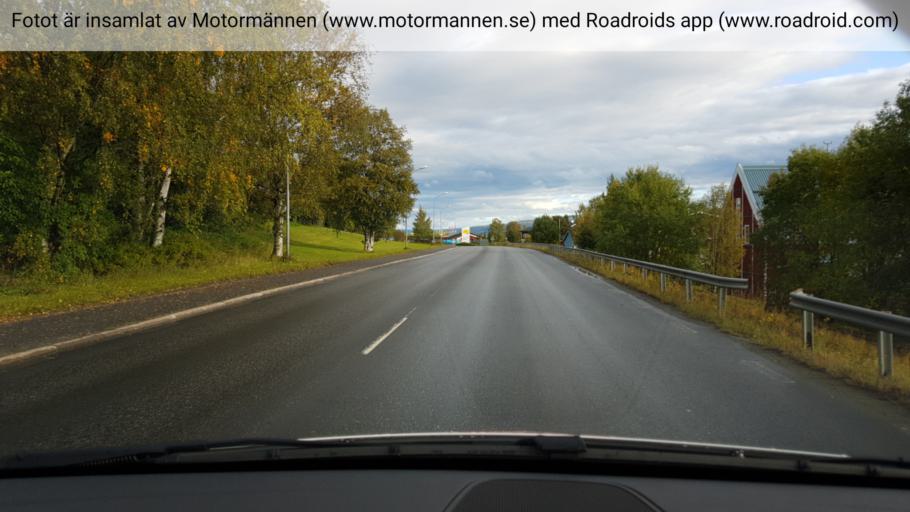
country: SE
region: Jaemtland
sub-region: Are Kommun
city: Jarpen
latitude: 63.3483
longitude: 13.4556
